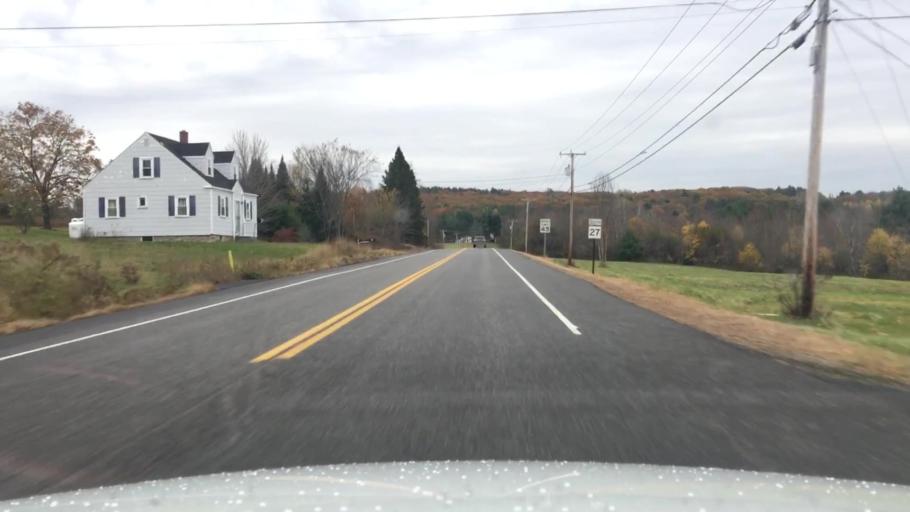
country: US
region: Maine
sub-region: Kennebec County
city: Pittston
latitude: 44.1925
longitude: -69.7484
